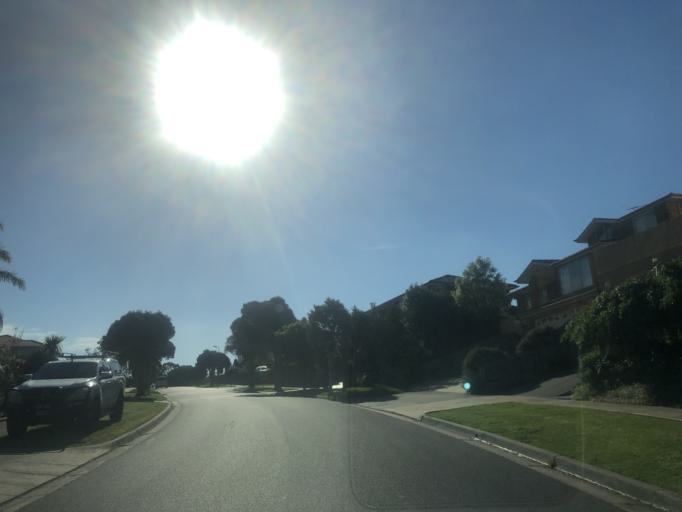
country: AU
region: Victoria
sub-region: Monash
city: Mulgrave
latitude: -37.9169
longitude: 145.1946
